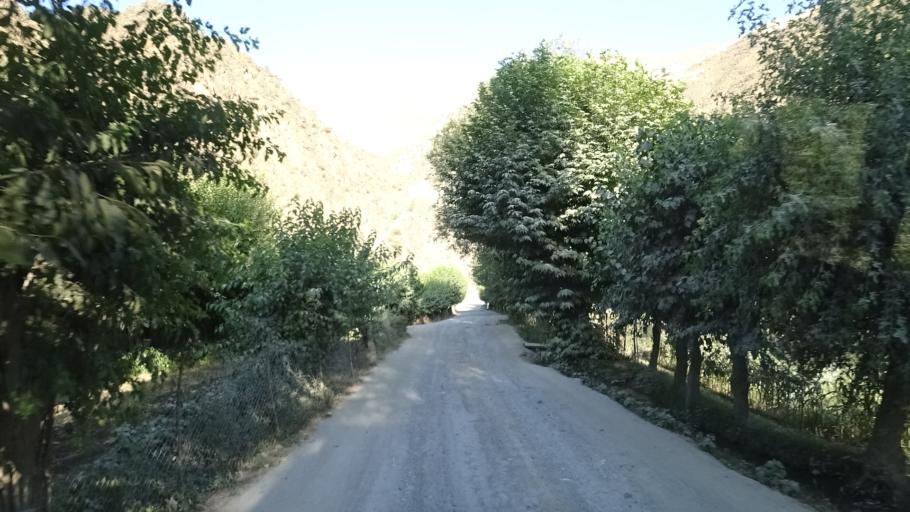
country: AF
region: Badakhshan
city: Maymay
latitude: 38.4770
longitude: 70.9643
